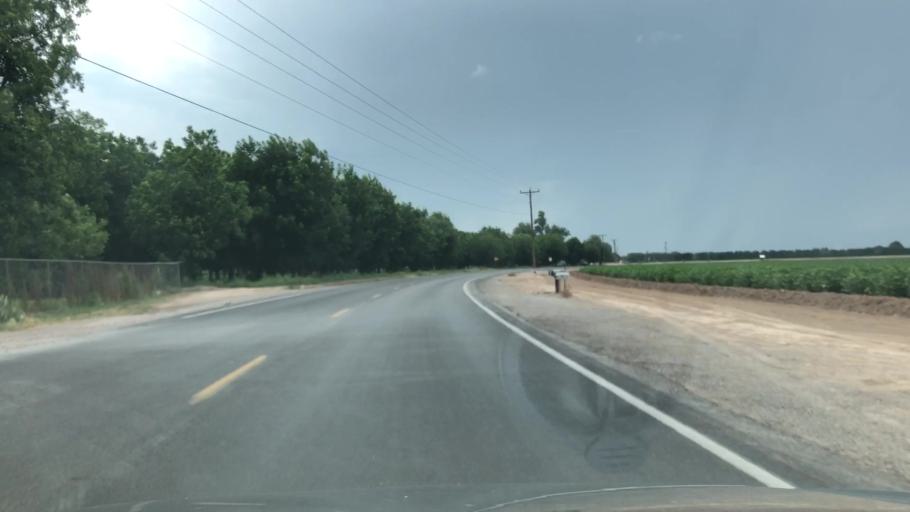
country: US
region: New Mexico
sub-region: Dona Ana County
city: La Union
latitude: 31.9707
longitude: -106.6518
